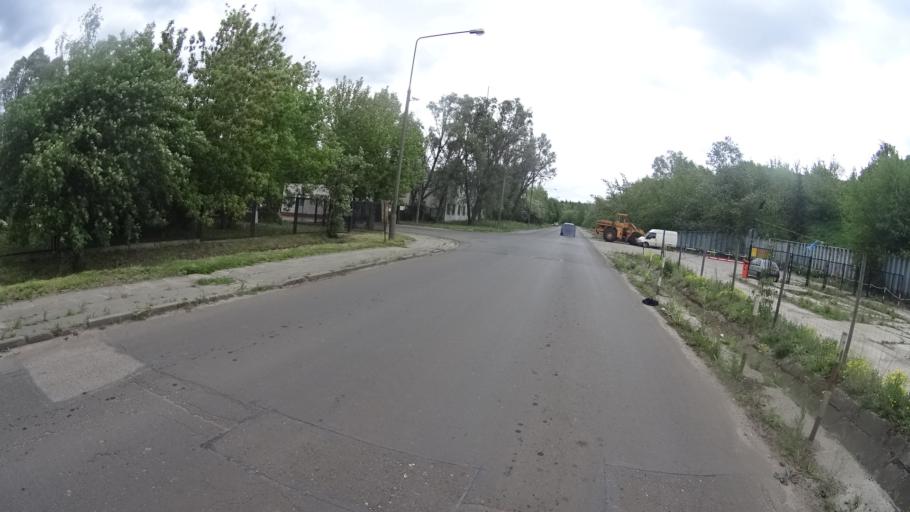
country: PL
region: Masovian Voivodeship
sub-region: Warszawa
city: Bemowo
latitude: 52.2800
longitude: 20.8794
